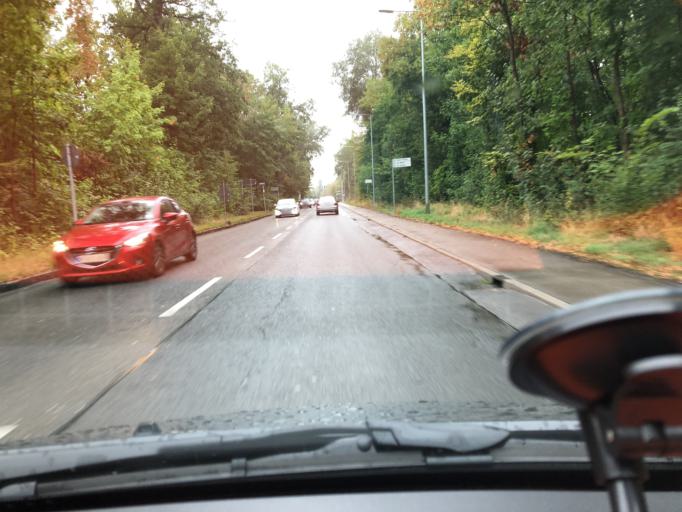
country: DE
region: Baden-Wuerttemberg
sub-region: Regierungsbezirk Stuttgart
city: Stuttgart
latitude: 48.7542
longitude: 9.1842
